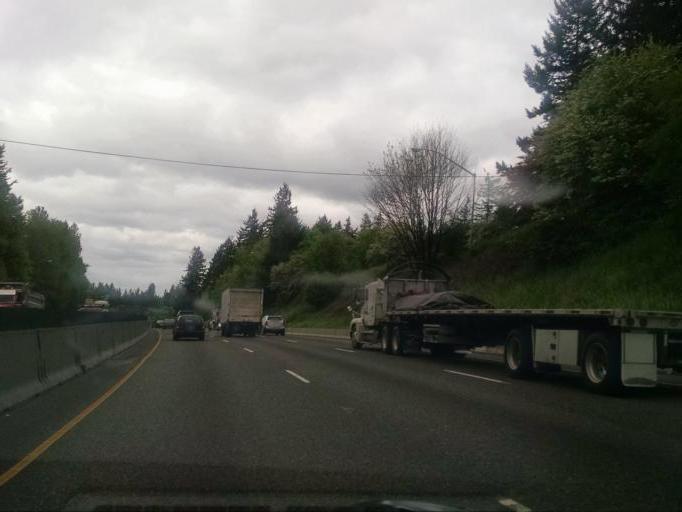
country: US
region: Oregon
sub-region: Washington County
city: Metzger
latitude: 45.4513
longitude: -122.7283
